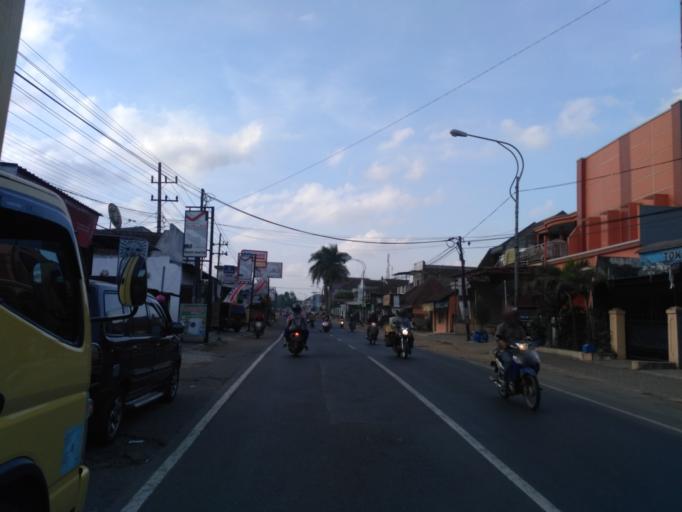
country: ID
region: East Java
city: Pakisaji
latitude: -8.0697
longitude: 112.5968
